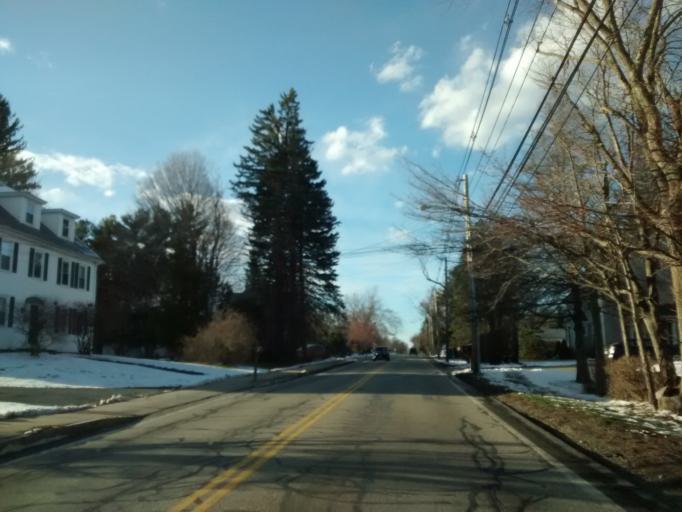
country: US
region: Massachusetts
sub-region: Middlesex County
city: Hopkinton
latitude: 42.2090
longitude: -71.5128
